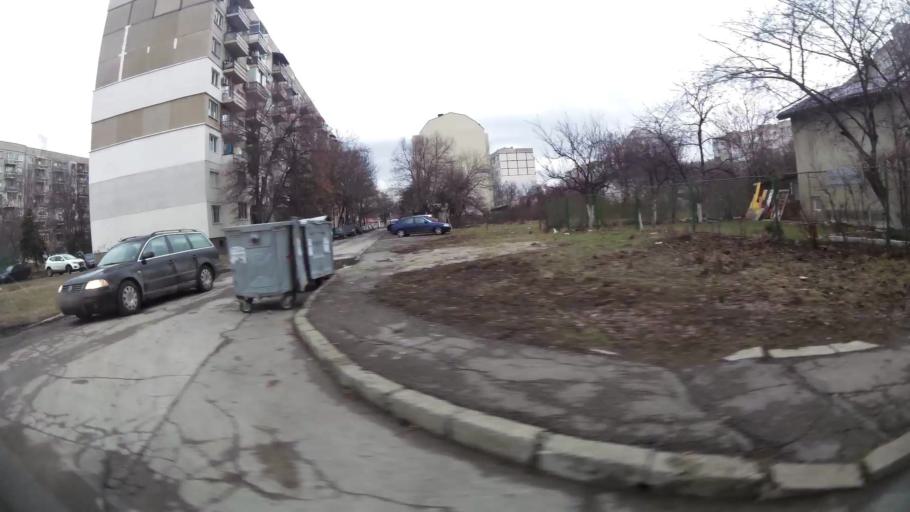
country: BG
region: Sofia-Capital
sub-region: Stolichna Obshtina
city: Sofia
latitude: 42.7244
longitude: 23.2983
